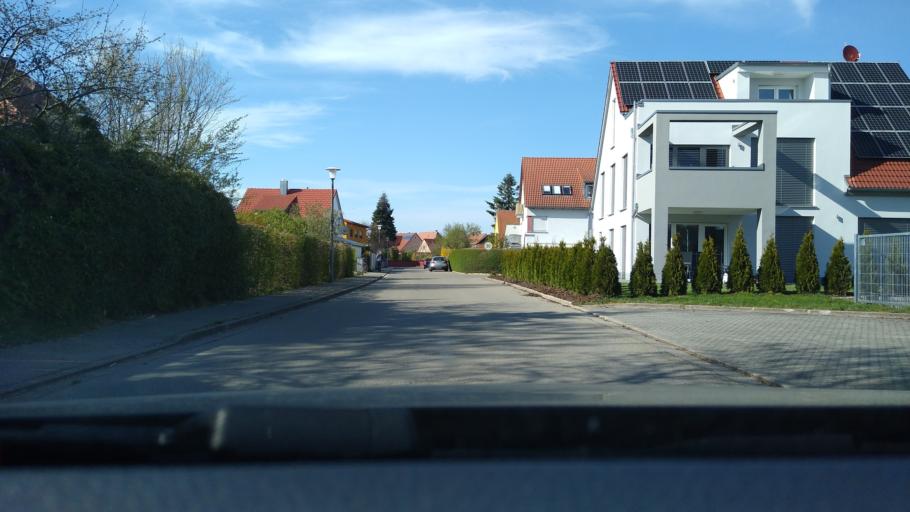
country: DE
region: Bavaria
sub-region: Regierungsbezirk Mittelfranken
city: Muhr am See
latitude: 49.1524
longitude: 10.7116
